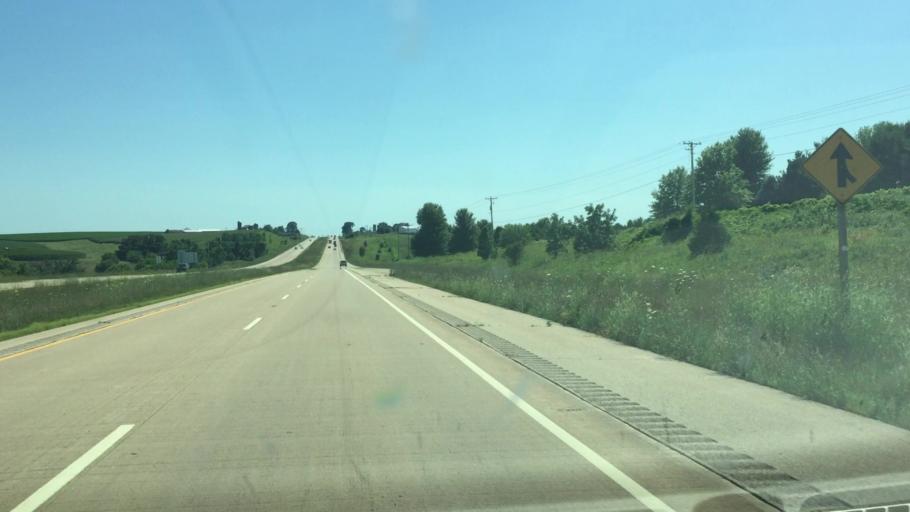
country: US
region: Wisconsin
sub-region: Grant County
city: Dickeyville
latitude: 42.6146
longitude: -90.5877
